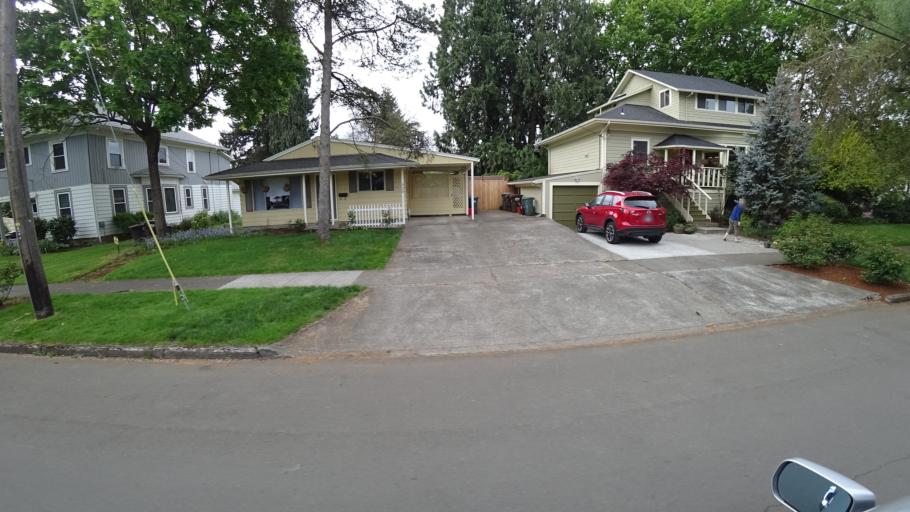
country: US
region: Oregon
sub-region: Washington County
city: Hillsboro
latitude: 45.5262
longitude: -122.9854
